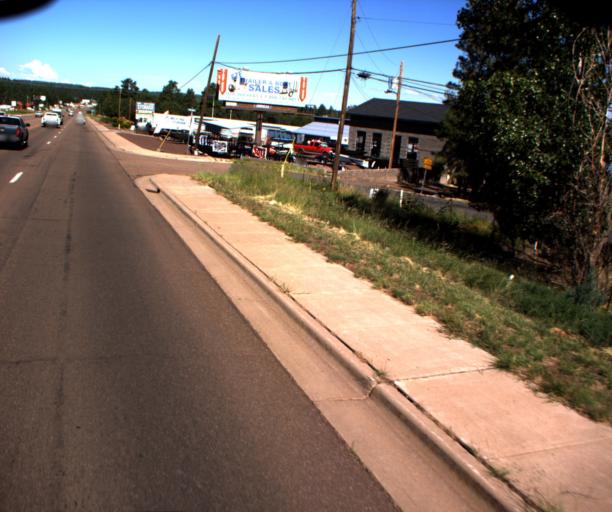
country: US
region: Arizona
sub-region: Navajo County
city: Lake of the Woods
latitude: 34.1662
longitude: -109.9934
